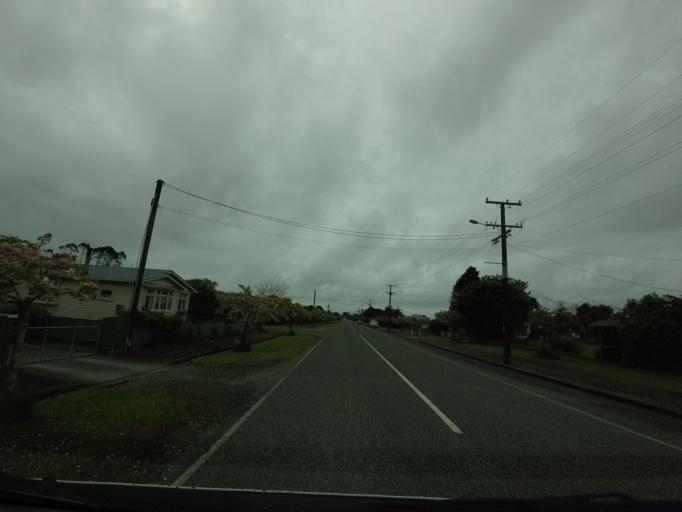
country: NZ
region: West Coast
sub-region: Westland District
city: Hokitika
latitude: -42.8960
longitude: 170.8143
